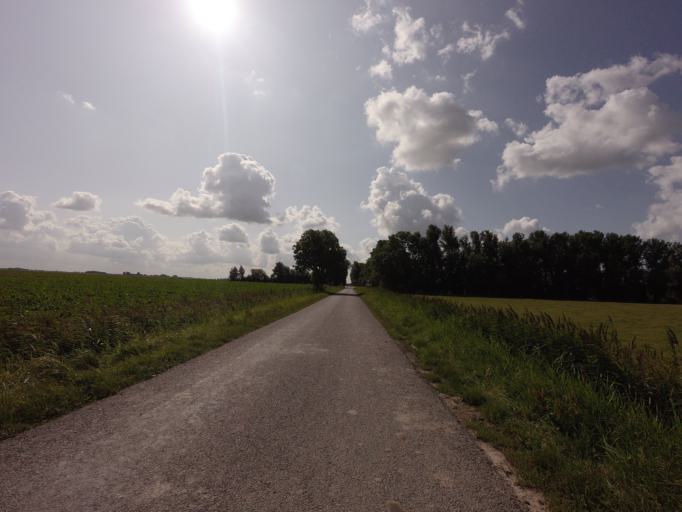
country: NL
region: Friesland
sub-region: Gemeente Het Bildt
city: Sint Annaparochie
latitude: 53.2797
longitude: 5.6755
